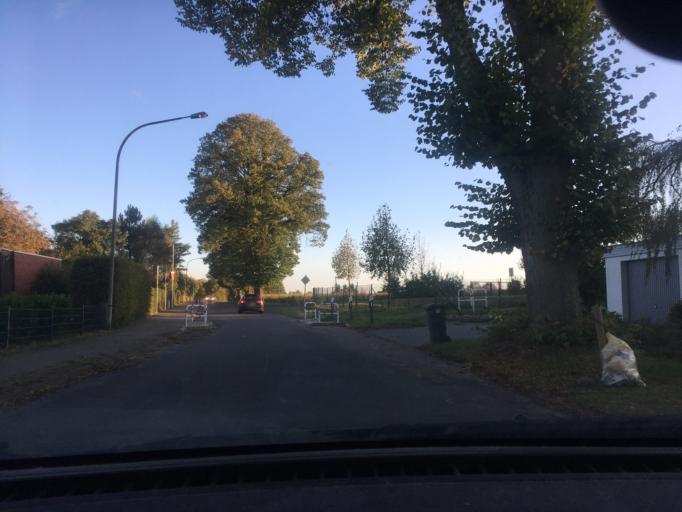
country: DE
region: Lower Saxony
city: Deutsch Evern
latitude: 53.2052
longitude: 10.4296
